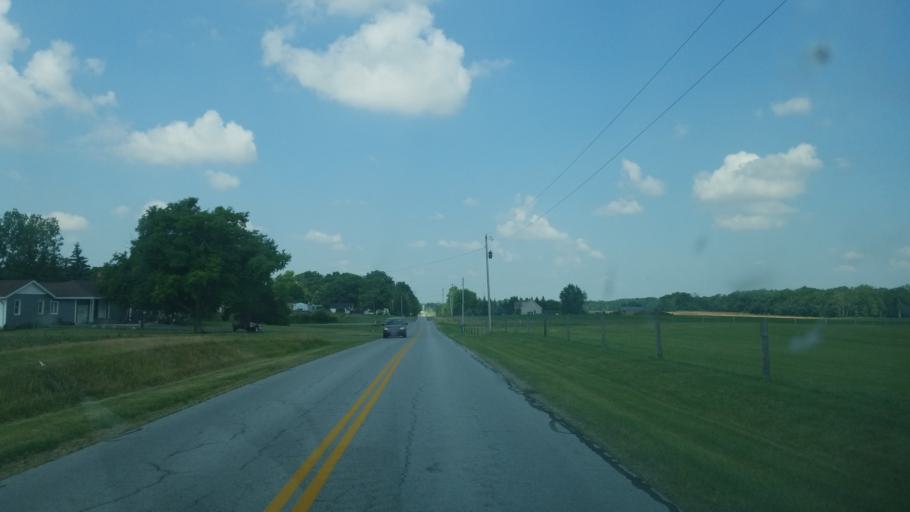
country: US
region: Ohio
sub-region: Auglaize County
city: Cridersville
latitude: 40.5714
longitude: -84.0586
